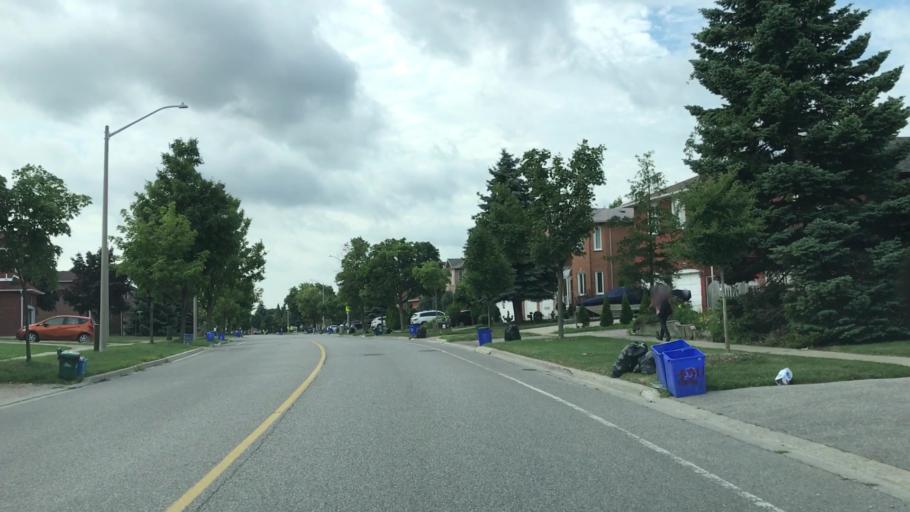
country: CA
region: Ontario
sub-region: York
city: Richmond Hill
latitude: 43.8518
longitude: -79.4016
